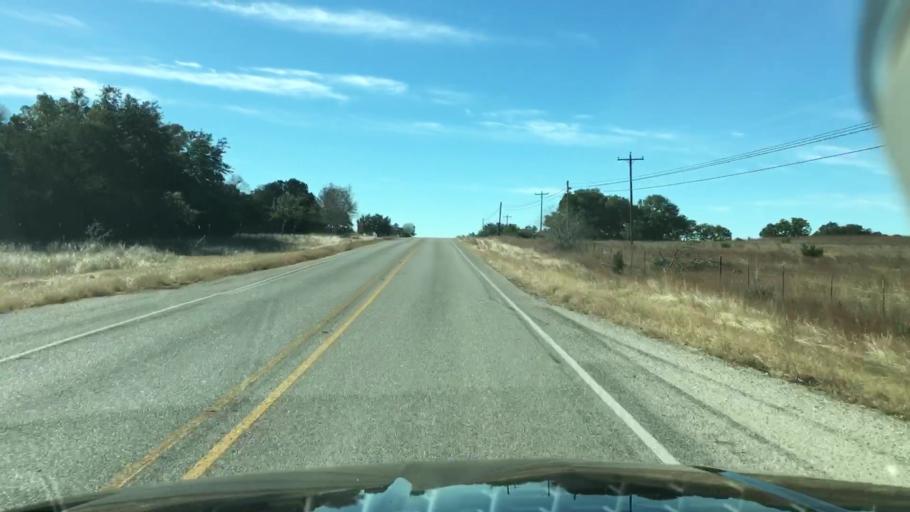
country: US
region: Texas
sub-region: Blanco County
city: Blanco
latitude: 30.1108
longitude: -98.3440
